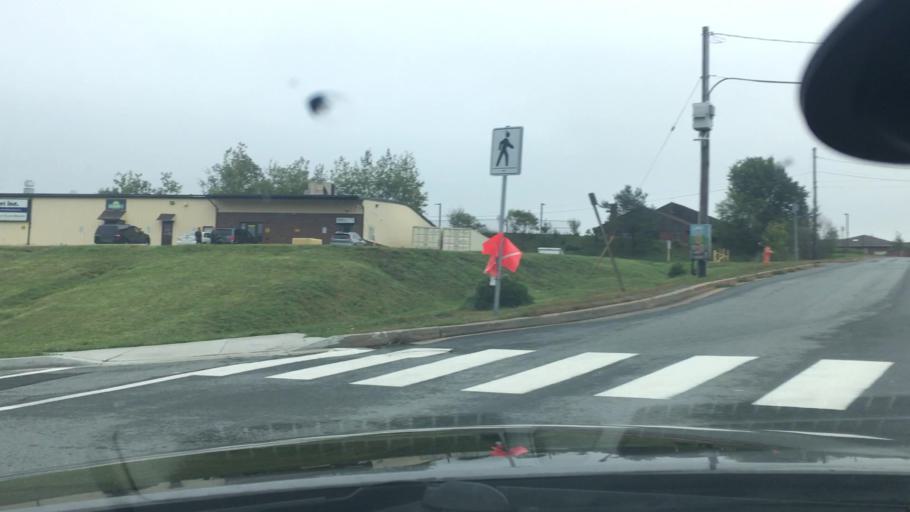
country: CA
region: Nova Scotia
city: Dartmouth
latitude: 44.7696
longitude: -63.6968
